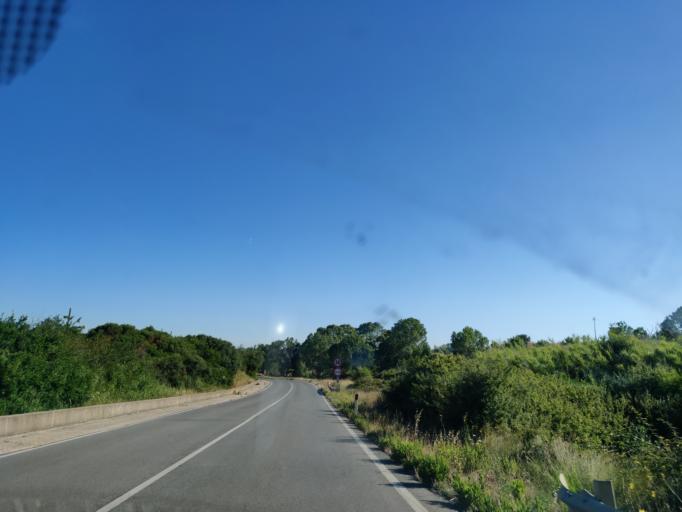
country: IT
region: Latium
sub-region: Citta metropolitana di Roma Capitale
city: Aurelia
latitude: 42.1453
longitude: 11.7889
